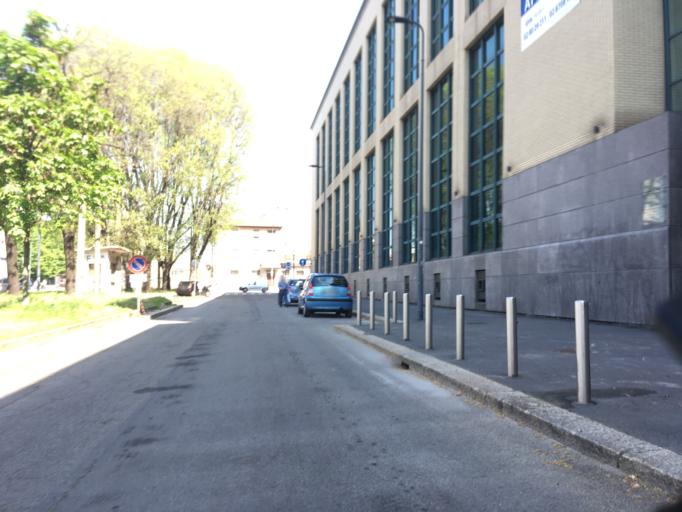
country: IT
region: Lombardy
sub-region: Citta metropolitana di Milano
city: Milano
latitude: 45.4420
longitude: 9.1996
